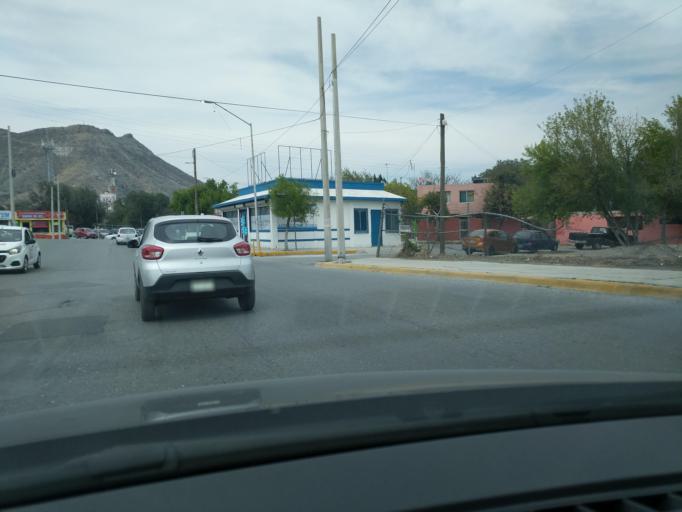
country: MX
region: Coahuila
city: Saltillo
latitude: 25.4277
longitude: -101.0169
